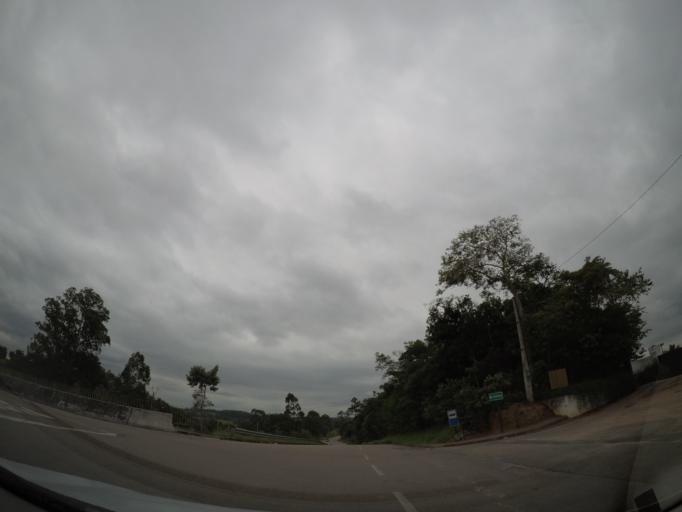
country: BR
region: Sao Paulo
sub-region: Louveira
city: Louveira
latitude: -23.1235
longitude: -46.9341
